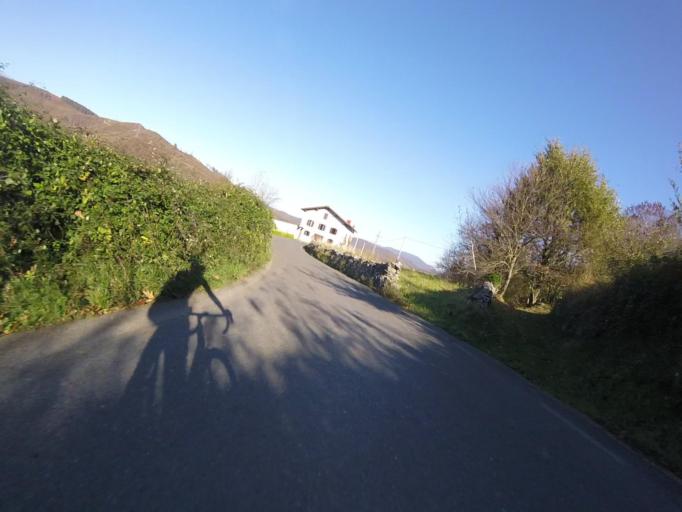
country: ES
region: Navarre
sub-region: Provincia de Navarra
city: Igantzi
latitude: 43.2310
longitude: -1.7036
